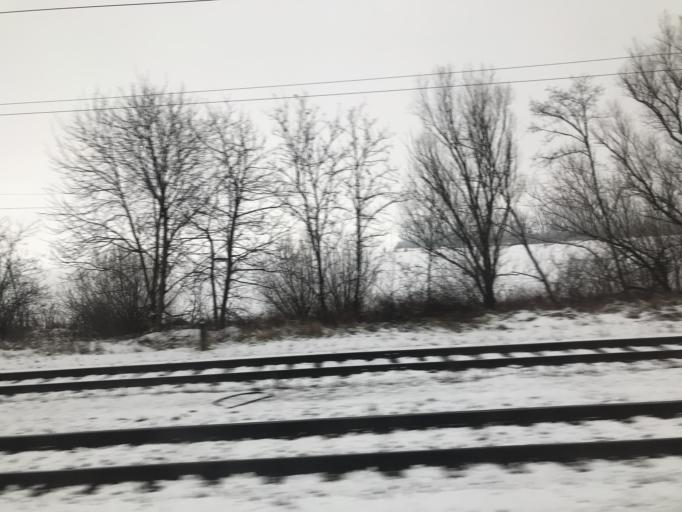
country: HU
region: Gyor-Moson-Sopron
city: Toltestava
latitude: 47.6887
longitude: 17.7471
